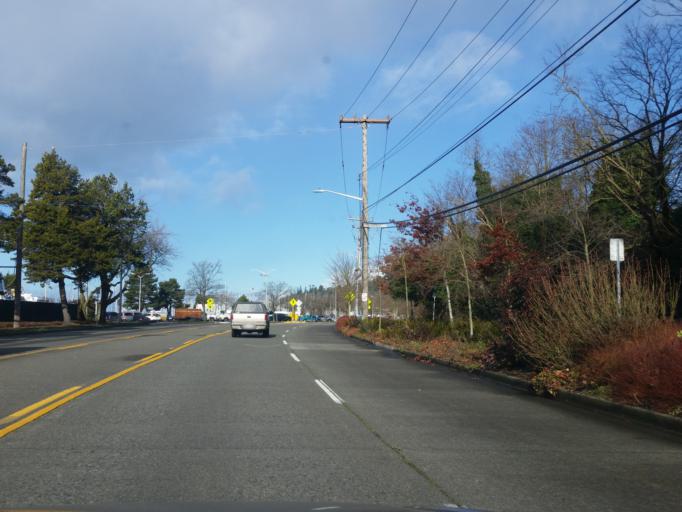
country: US
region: Washington
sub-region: King County
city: Shoreline
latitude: 47.6767
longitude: -122.4064
